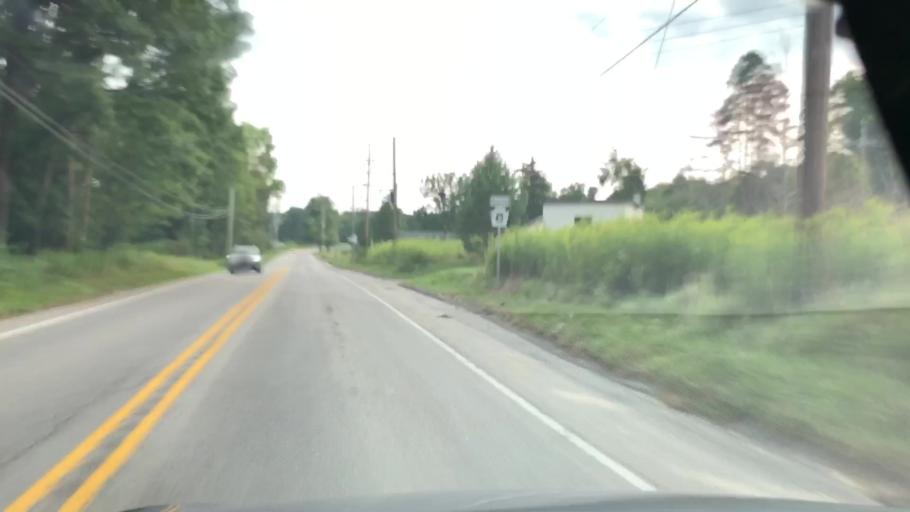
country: US
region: Pennsylvania
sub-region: Crawford County
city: Titusville
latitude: 41.5477
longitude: -79.7029
